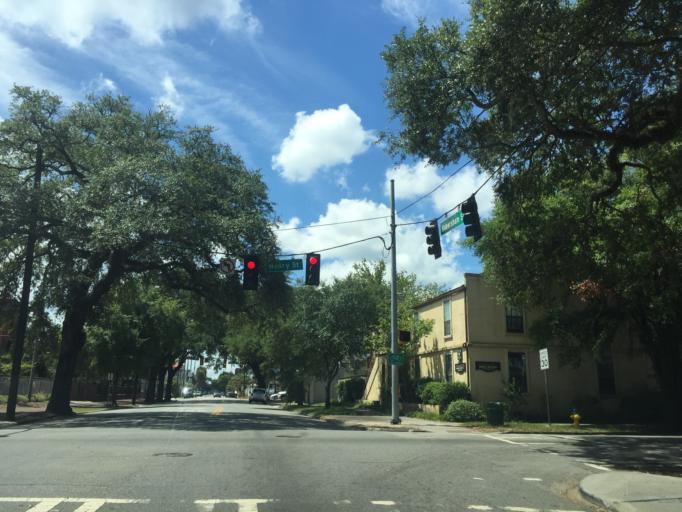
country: US
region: Georgia
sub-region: Chatham County
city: Savannah
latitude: 32.0622
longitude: -81.0935
